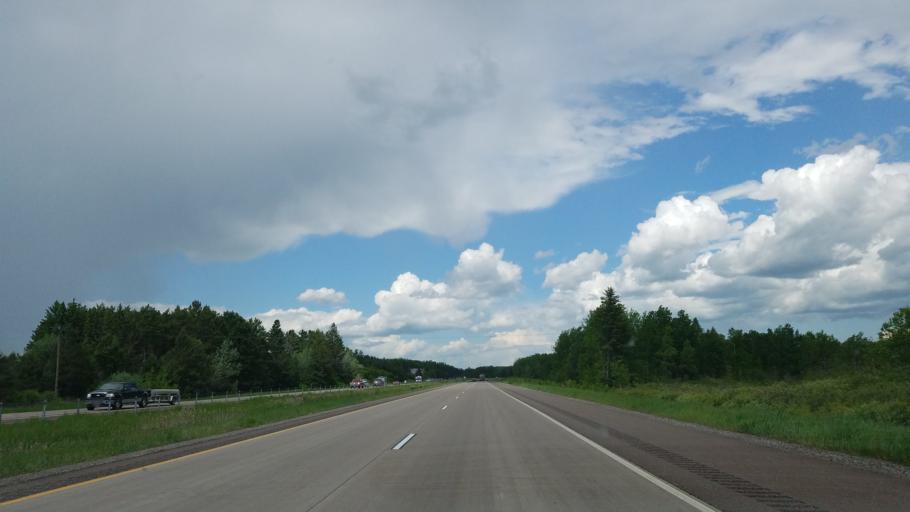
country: US
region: Minnesota
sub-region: Carlton County
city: Moose Lake
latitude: 46.4783
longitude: -92.7124
